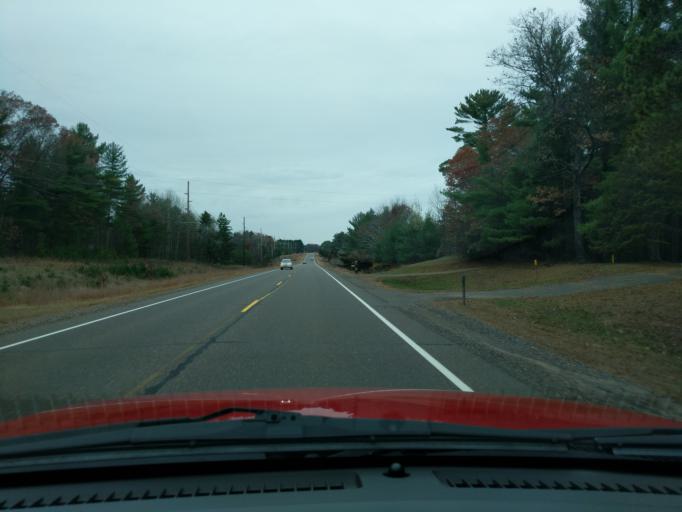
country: US
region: Wisconsin
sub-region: Burnett County
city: Siren
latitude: 45.8116
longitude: -92.2261
